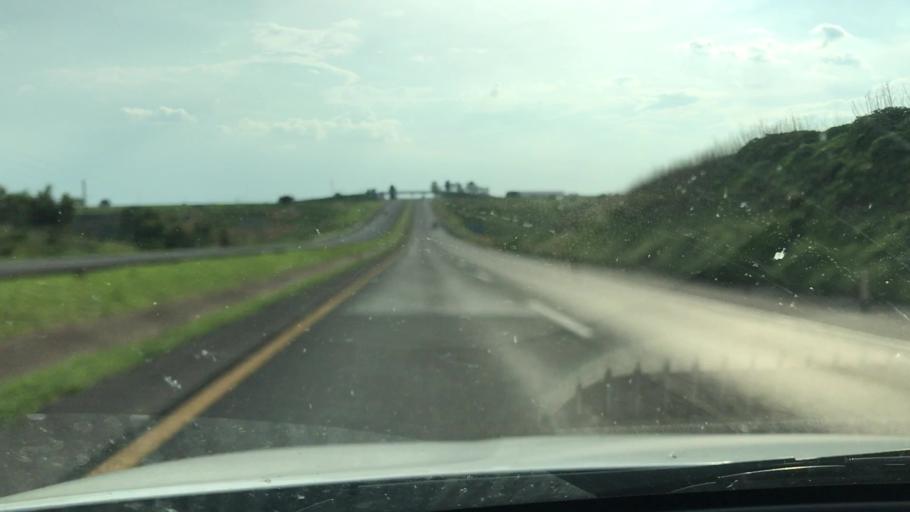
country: MX
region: Guanajuato
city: Penjamo
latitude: 20.3860
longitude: -101.7774
